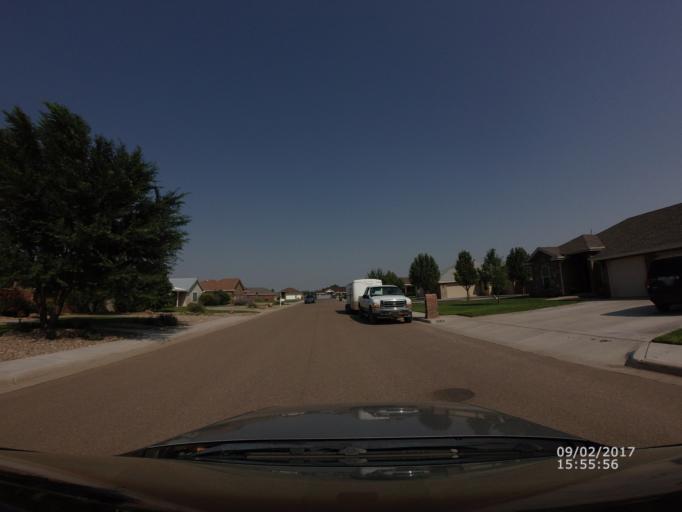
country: US
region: New Mexico
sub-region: Curry County
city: Clovis
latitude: 34.4491
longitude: -103.1897
